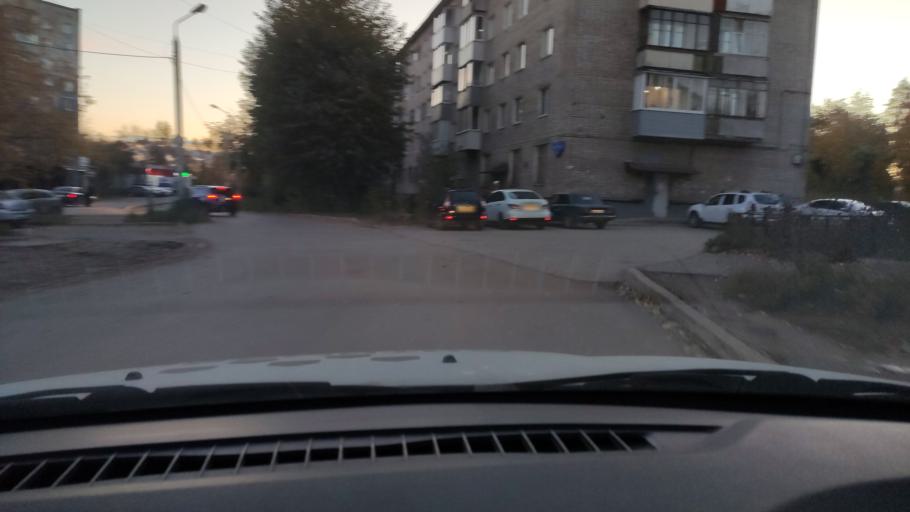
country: RU
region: Perm
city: Perm
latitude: 57.9636
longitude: 56.2322
